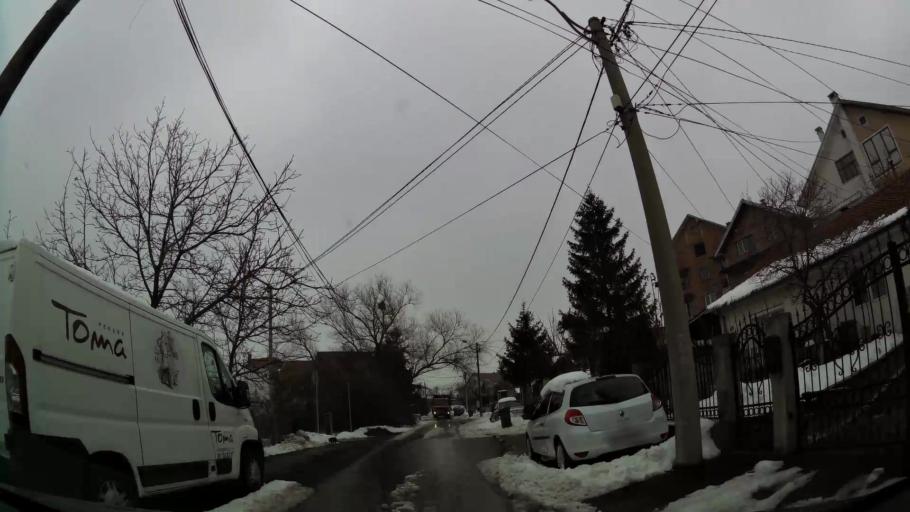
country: RS
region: Central Serbia
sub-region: Belgrade
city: Zvezdara
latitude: 44.7423
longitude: 20.5087
